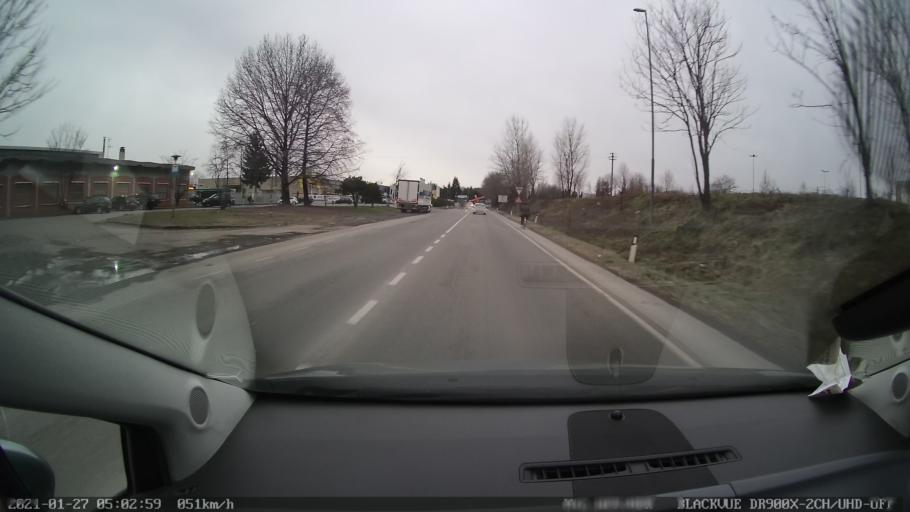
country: IT
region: Lombardy
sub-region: Provincia di Varese
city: Tradate
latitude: 45.7026
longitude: 8.9075
